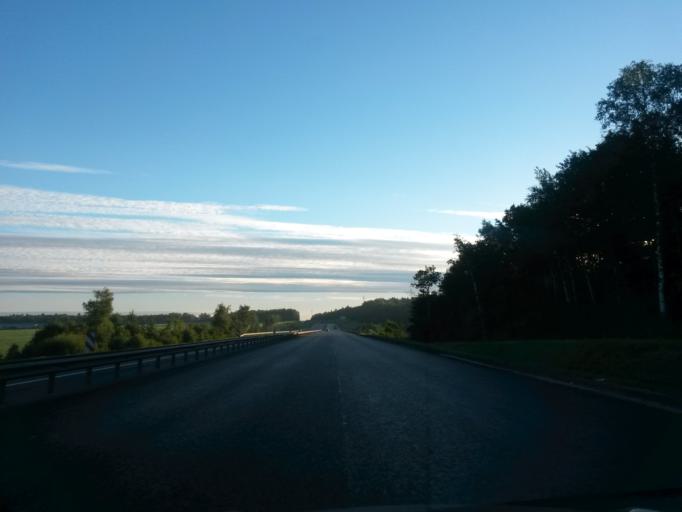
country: RU
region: Moskovskaya
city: Svatkovo
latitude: 56.3719
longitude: 38.3098
